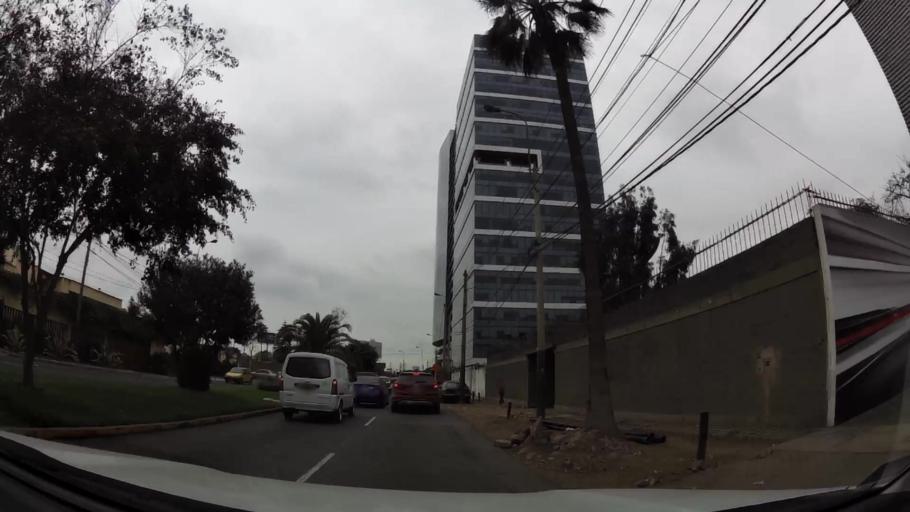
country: PE
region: Lima
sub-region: Lima
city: La Molina
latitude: -12.0984
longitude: -76.9716
